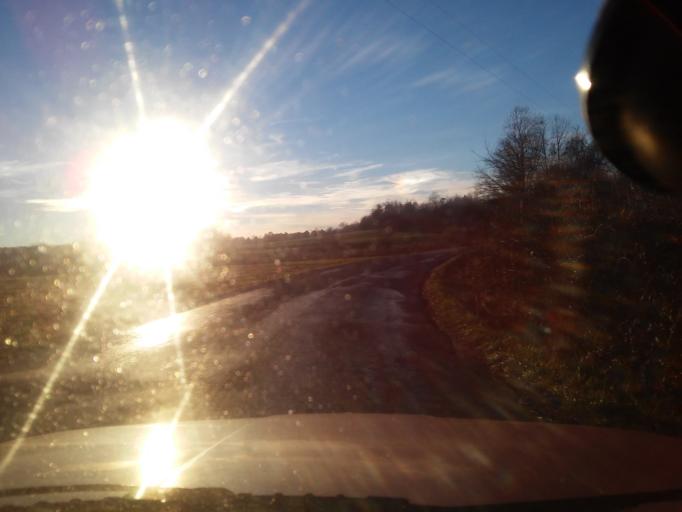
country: US
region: Virginia
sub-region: Henrico County
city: Wyndham
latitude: 37.7200
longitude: -77.7171
